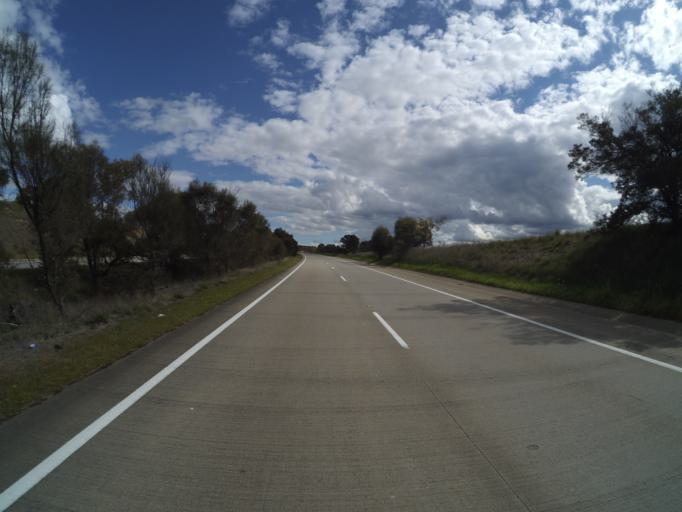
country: AU
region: New South Wales
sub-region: Yass Valley
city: Murrumbateman
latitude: -34.7885
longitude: 149.1761
